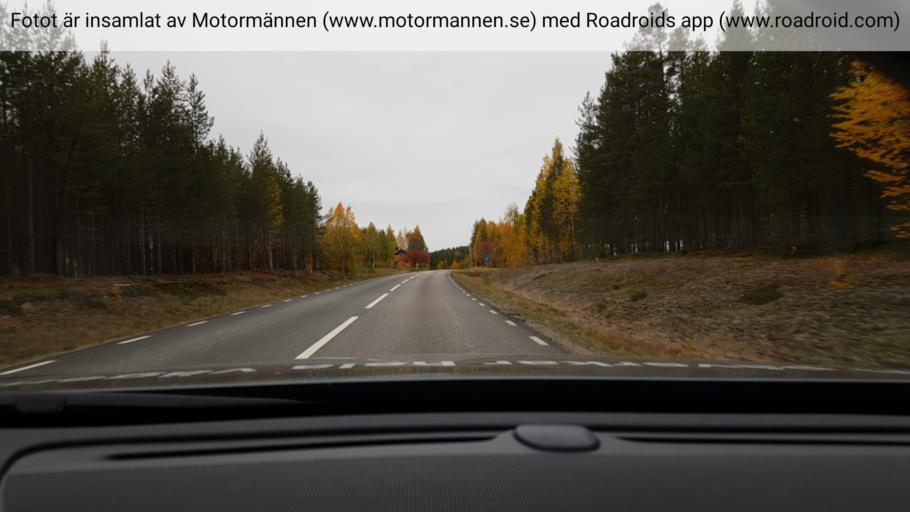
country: SE
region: Norrbotten
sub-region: Overkalix Kommun
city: OEverkalix
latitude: 66.5280
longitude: 22.7618
